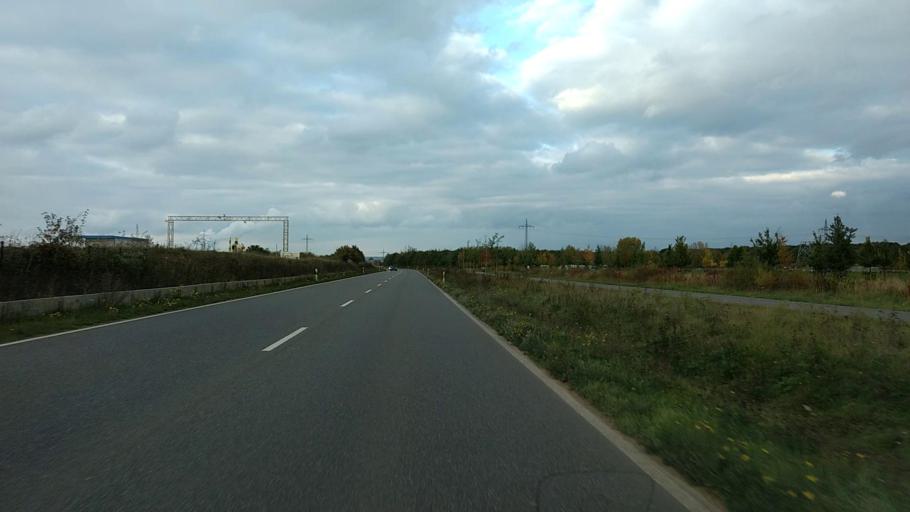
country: DE
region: North Rhine-Westphalia
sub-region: Regierungsbezirk Koln
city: Kerpen
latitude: 50.8791
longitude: 6.6411
